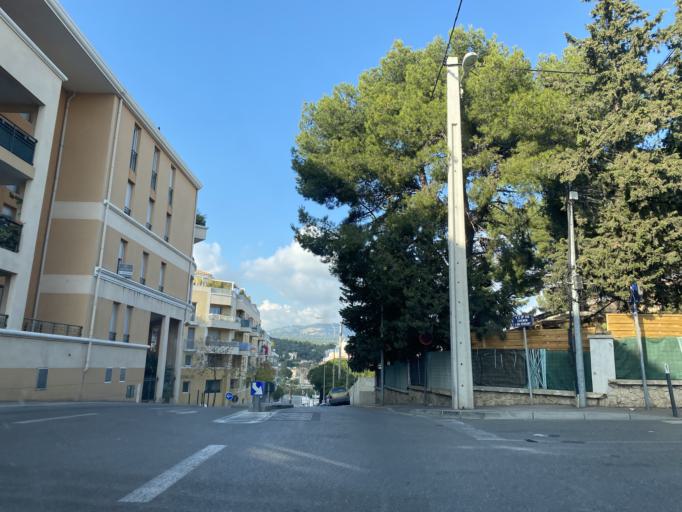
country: FR
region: Provence-Alpes-Cote d'Azur
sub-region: Departement du Var
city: La Seyne-sur-Mer
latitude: 43.1126
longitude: 5.8730
